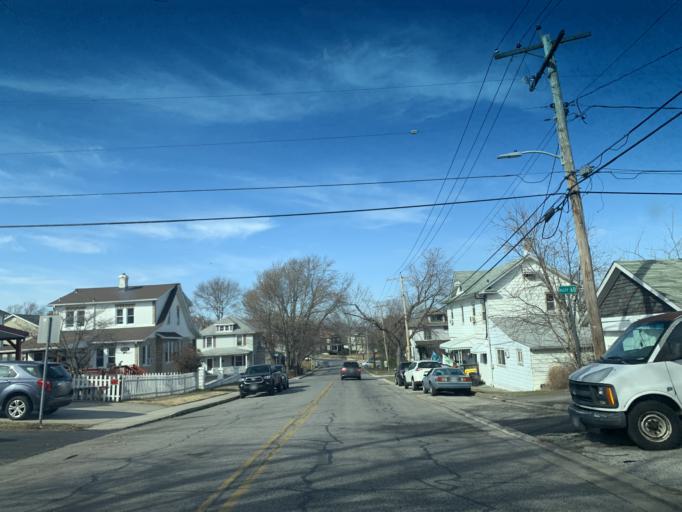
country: US
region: Maryland
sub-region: Anne Arundel County
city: Brooklyn Park
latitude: 39.2314
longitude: -76.6145
